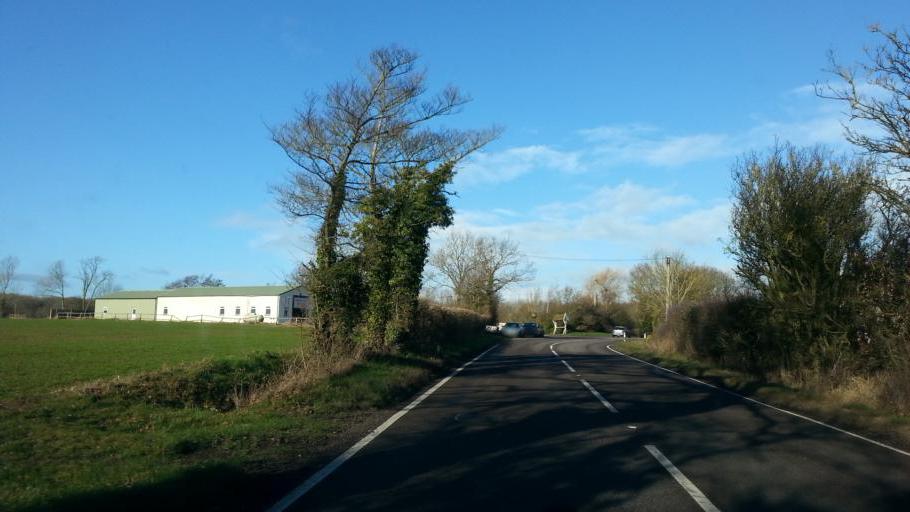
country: GB
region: England
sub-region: Suffolk
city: Halesworth
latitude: 52.3191
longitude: 1.5194
